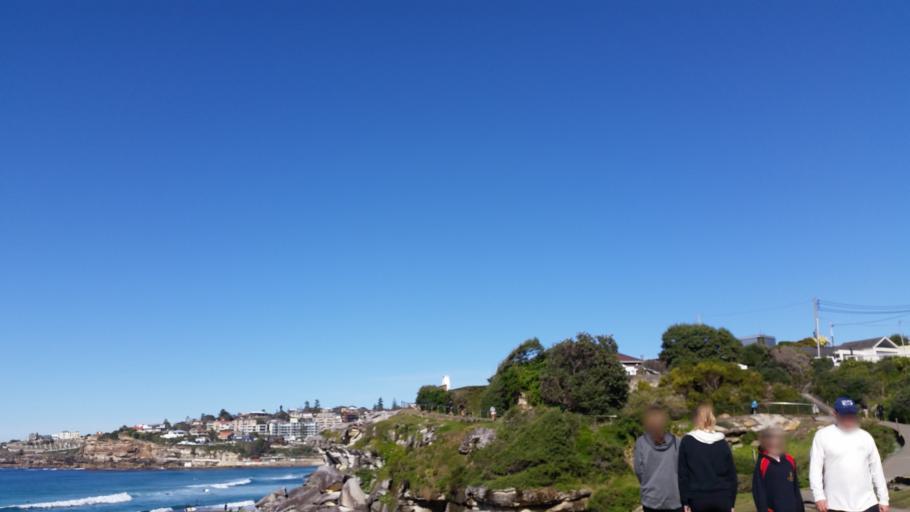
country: AU
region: New South Wales
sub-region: Waverley
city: Bronte
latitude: -33.8992
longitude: 151.2725
